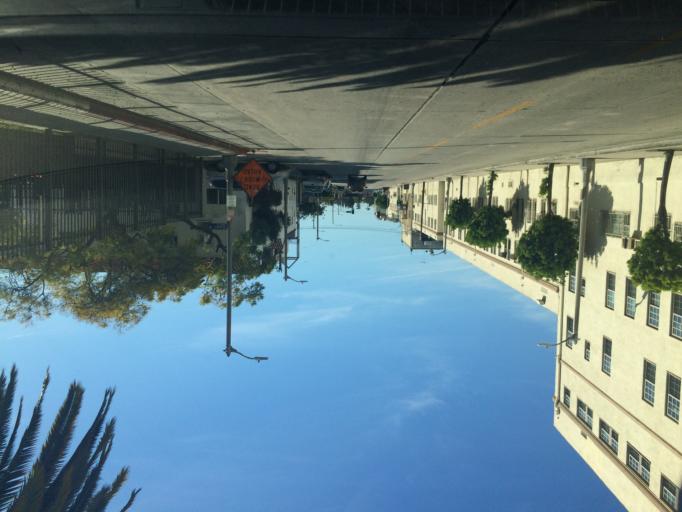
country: US
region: California
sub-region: Los Angeles County
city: Hollywood
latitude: 34.0865
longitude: -118.3223
